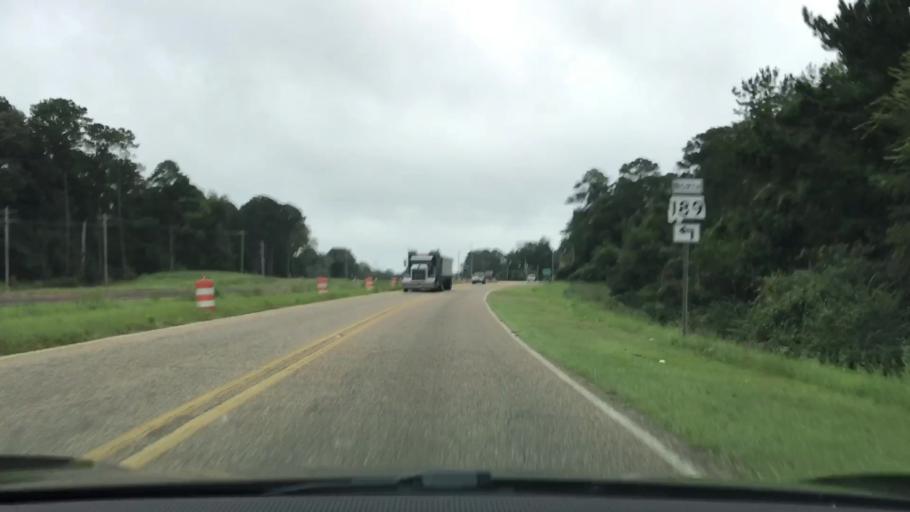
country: US
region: Alabama
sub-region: Coffee County
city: Elba
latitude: 31.4263
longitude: -86.0772
